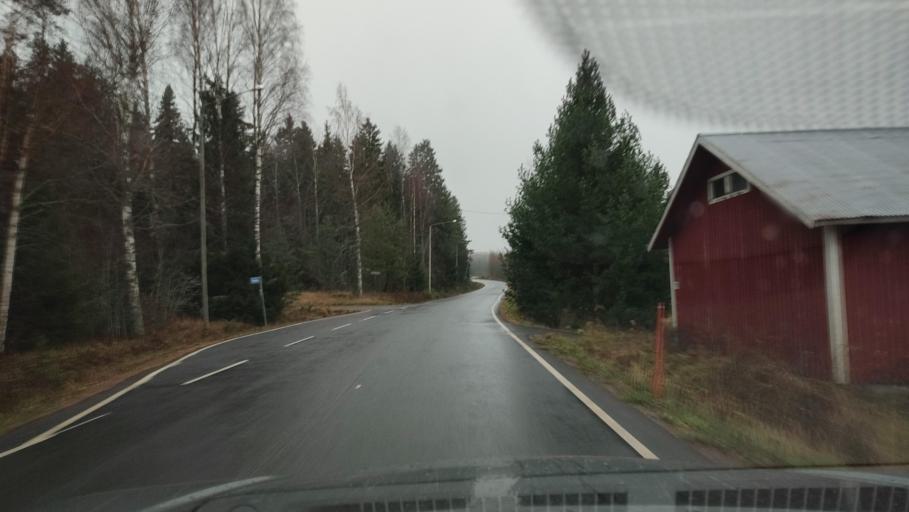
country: FI
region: Southern Ostrobothnia
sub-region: Suupohja
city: Karijoki
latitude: 62.1420
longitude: 21.6858
